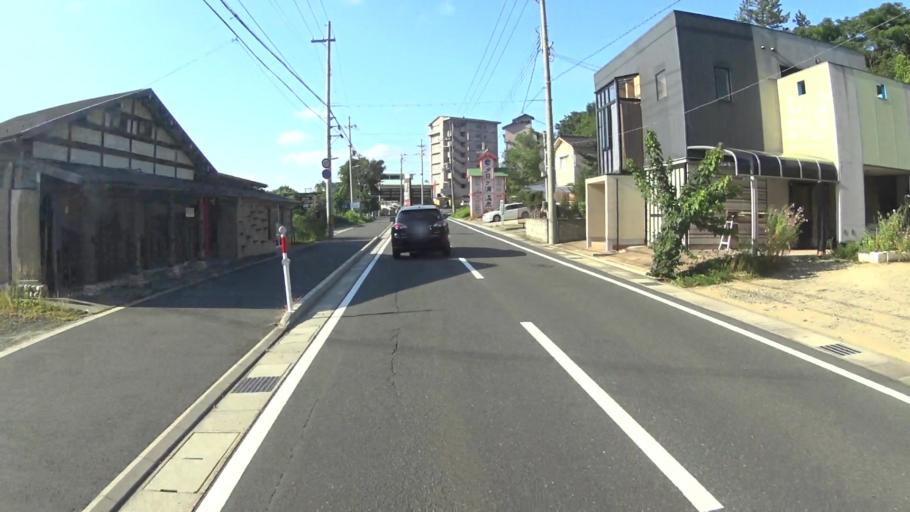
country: JP
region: Hyogo
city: Toyooka
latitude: 35.6574
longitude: 134.9677
